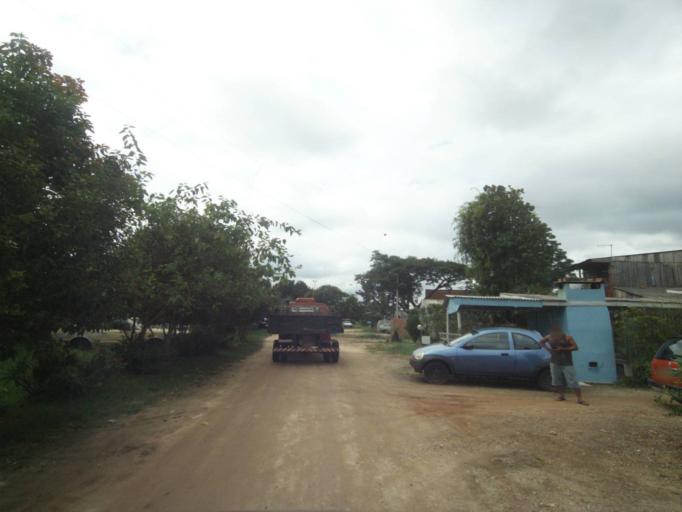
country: BR
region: Parana
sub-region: Pinhais
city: Pinhais
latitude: -25.4515
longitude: -49.1983
